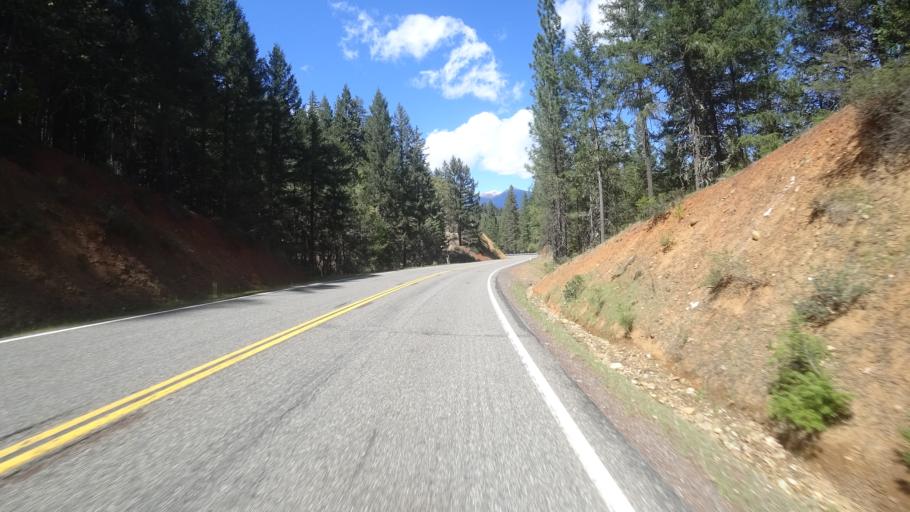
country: US
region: California
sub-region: Trinity County
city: Weaverville
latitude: 40.7900
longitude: -122.8933
